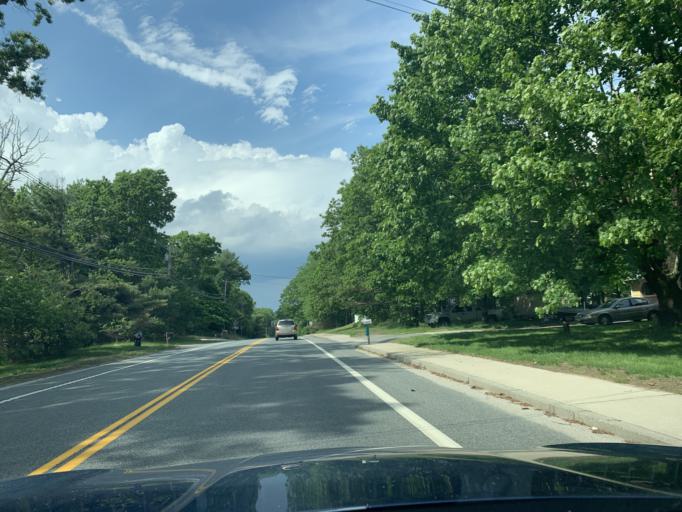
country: US
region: Rhode Island
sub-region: Kent County
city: Coventry
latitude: 41.6818
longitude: -71.6940
